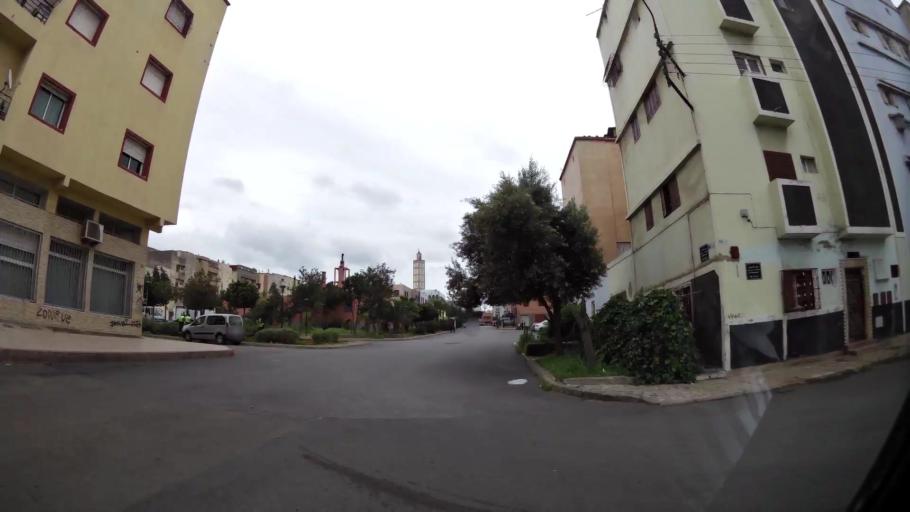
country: MA
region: Grand Casablanca
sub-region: Casablanca
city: Casablanca
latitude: 33.5701
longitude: -7.5551
